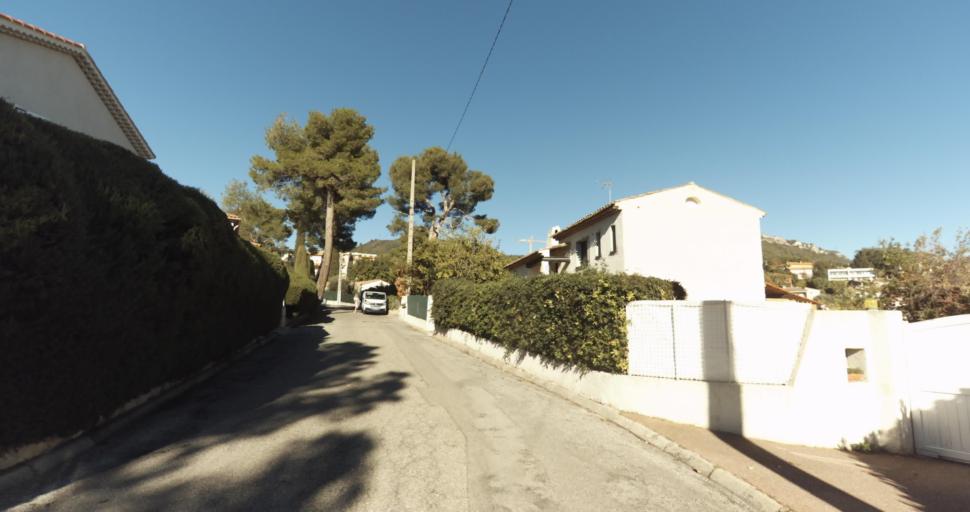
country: FR
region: Provence-Alpes-Cote d'Azur
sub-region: Departement des Alpes-Maritimes
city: Vence
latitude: 43.7183
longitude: 7.1035
